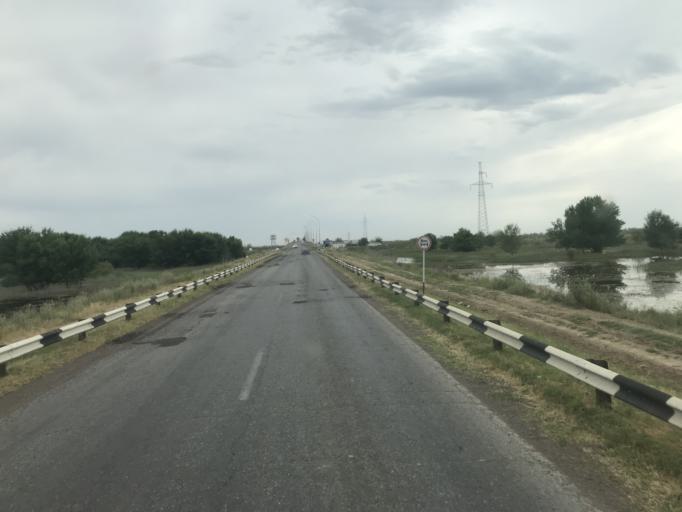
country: KZ
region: Ongtustik Qazaqstan
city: Ilyich
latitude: 41.0327
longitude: 68.5236
